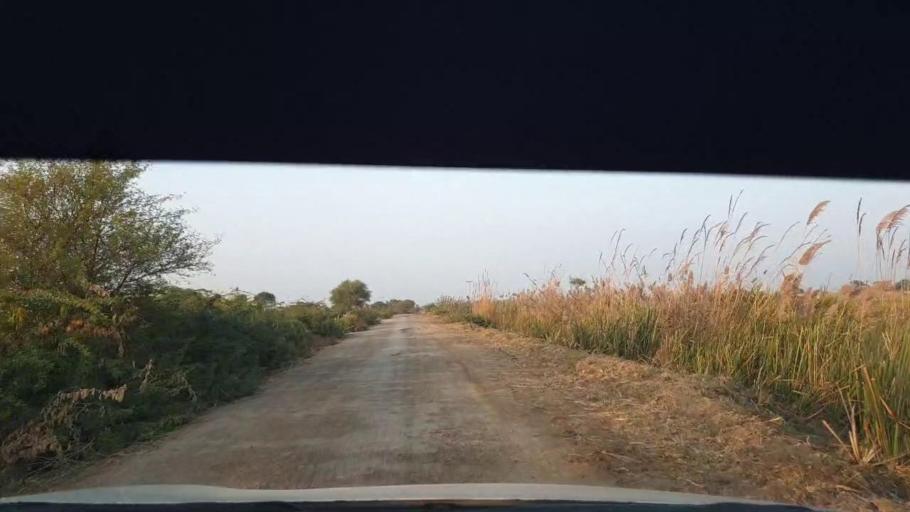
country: PK
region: Sindh
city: Berani
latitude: 25.7518
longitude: 68.9817
